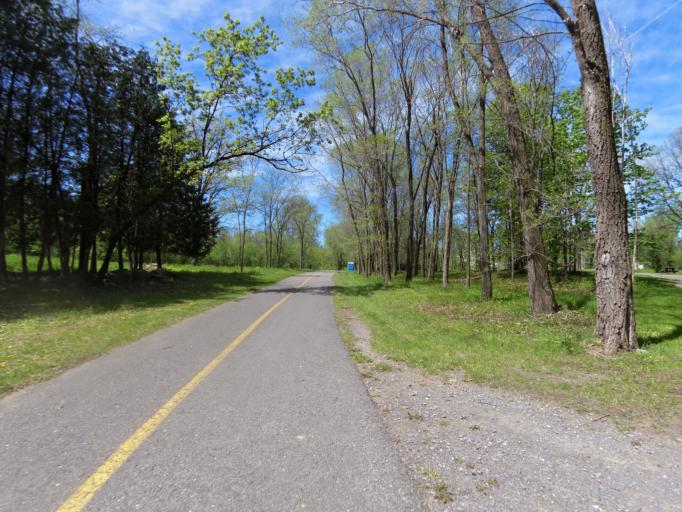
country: CA
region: Ontario
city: Bells Corners
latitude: 45.3870
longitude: -75.7982
